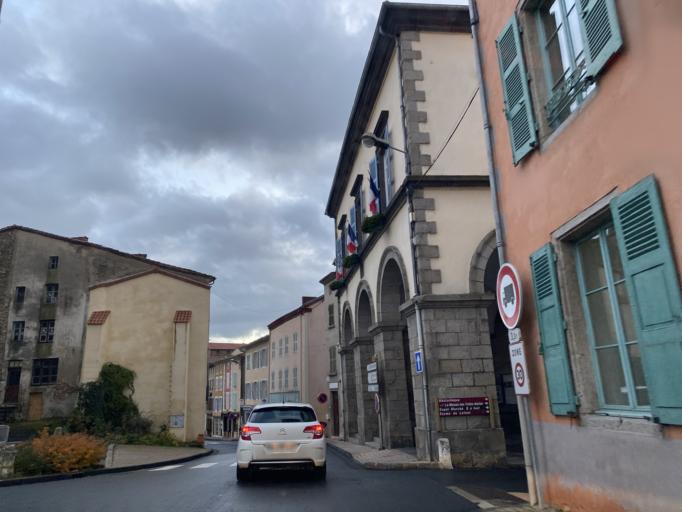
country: FR
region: Auvergne
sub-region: Departement du Puy-de-Dome
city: Cunlhat
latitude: 45.6329
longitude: 3.5596
